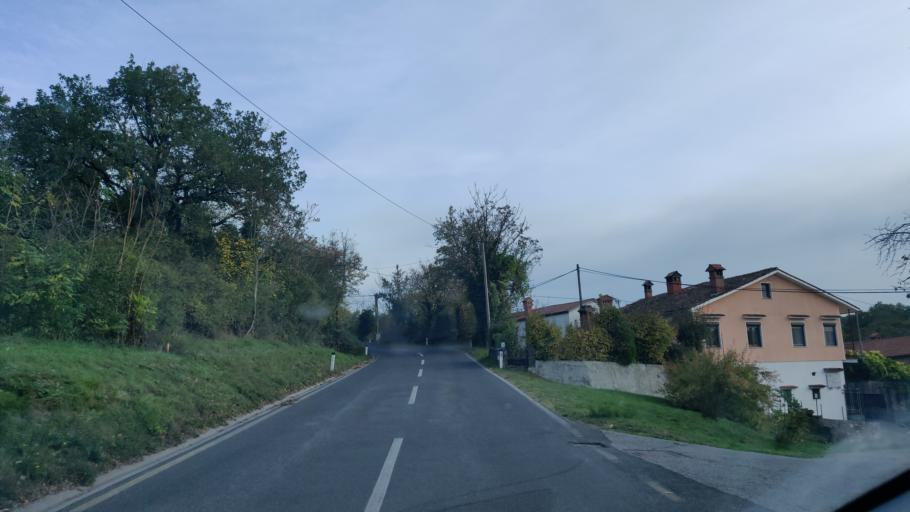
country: SI
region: Komen
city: Komen
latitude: 45.8173
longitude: 13.7699
